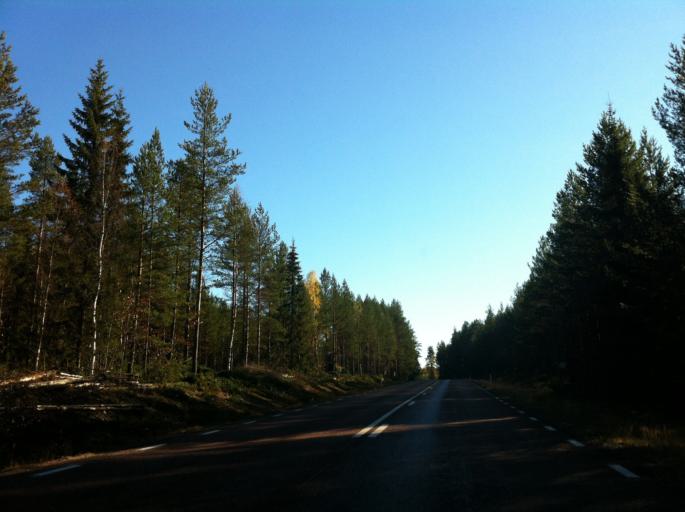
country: SE
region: Dalarna
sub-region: Alvdalens Kommun
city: AElvdalen
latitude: 61.1688
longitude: 14.1072
